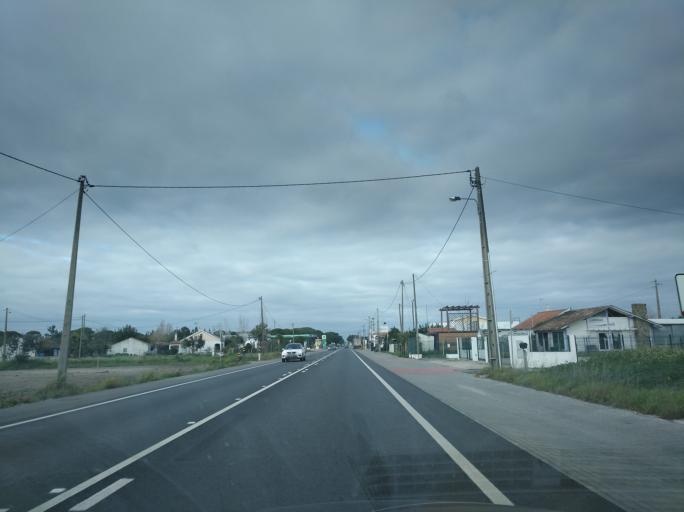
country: PT
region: Setubal
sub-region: Grandola
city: Grandola
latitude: 38.2176
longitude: -8.5582
